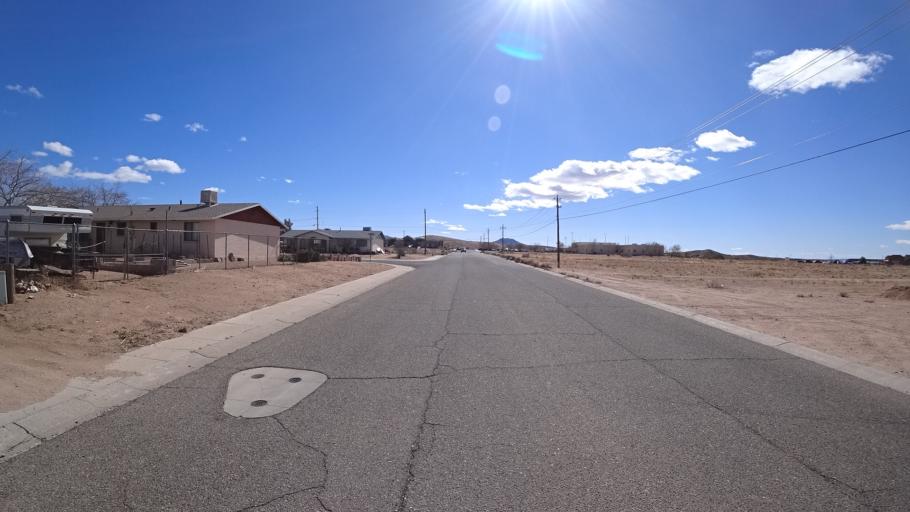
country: US
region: Arizona
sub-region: Mohave County
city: Kingman
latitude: 35.1917
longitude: -114.0136
